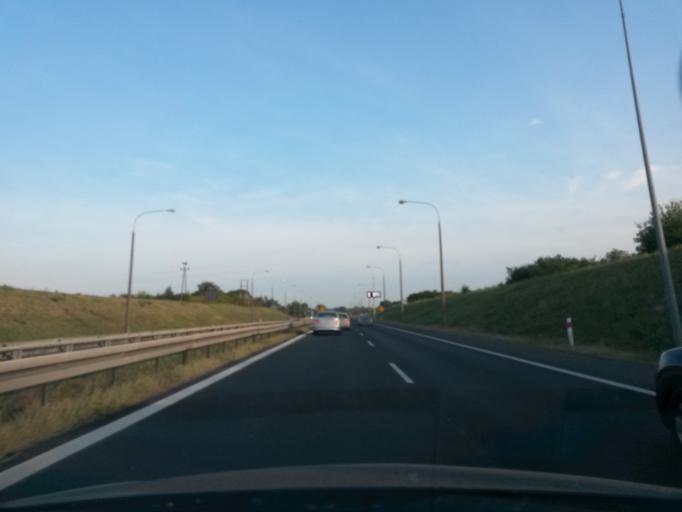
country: PL
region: Masovian Voivodeship
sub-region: Powiat nowodworski
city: Zakroczym
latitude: 52.4320
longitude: 20.6517
